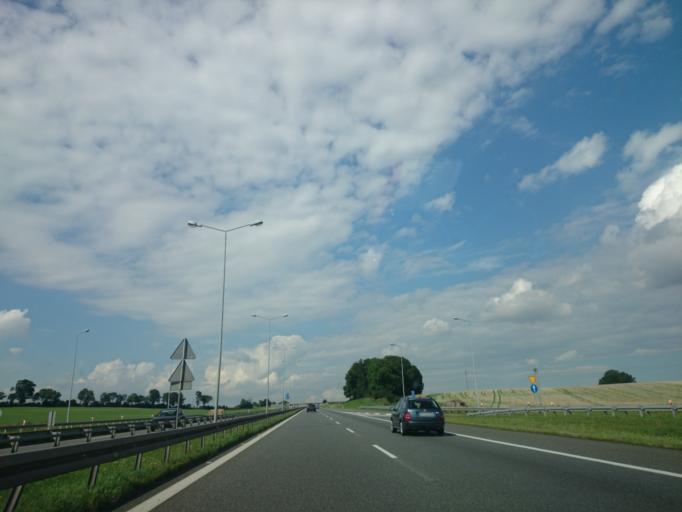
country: PL
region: Opole Voivodeship
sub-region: Powiat strzelecki
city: Strzelce Opolskie
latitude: 50.4592
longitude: 18.2690
